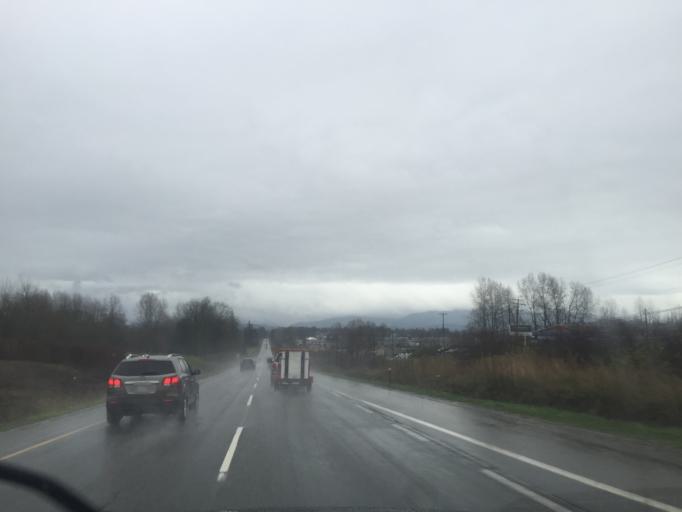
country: CA
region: British Columbia
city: Aldergrove
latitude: 49.0533
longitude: -122.3713
